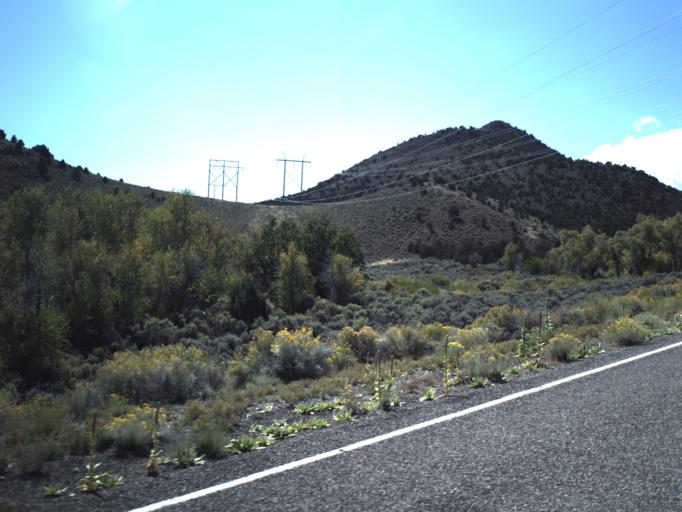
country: US
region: Utah
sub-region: Piute County
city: Junction
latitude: 38.2595
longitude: -112.2626
